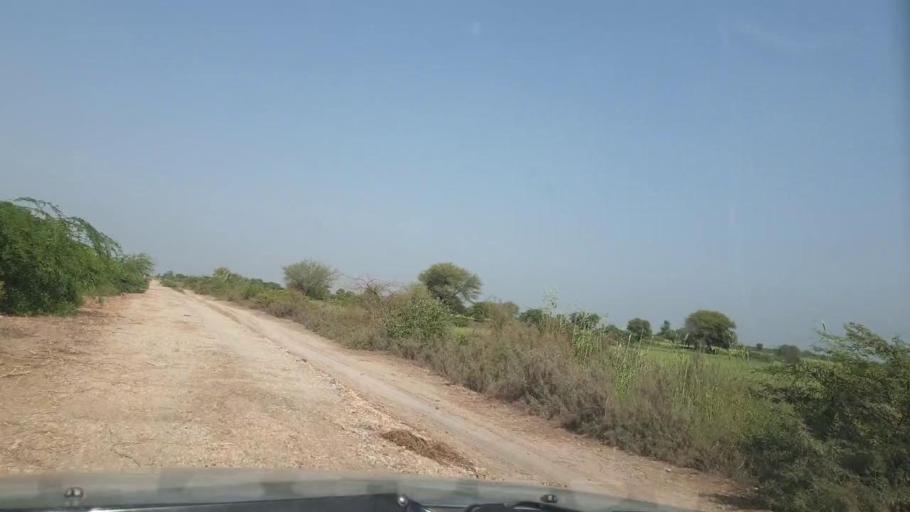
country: PK
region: Sindh
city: Tando Ghulam Ali
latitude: 25.0899
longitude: 68.8021
